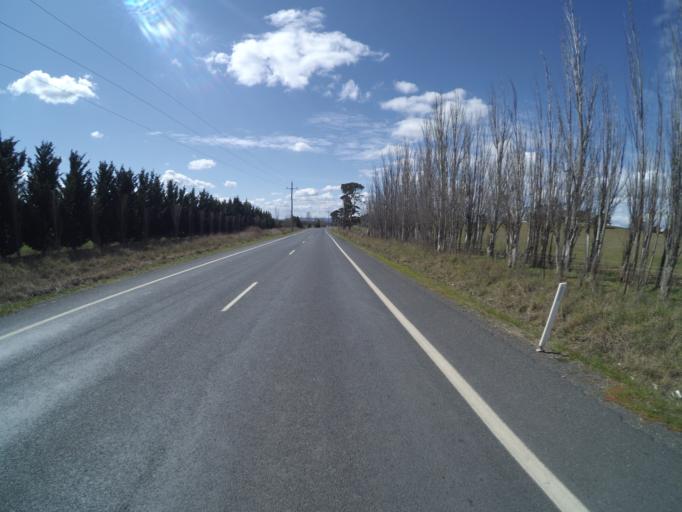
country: AU
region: New South Wales
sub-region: Goulburn Mulwaree
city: Goulburn
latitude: -34.7898
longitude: 149.6997
